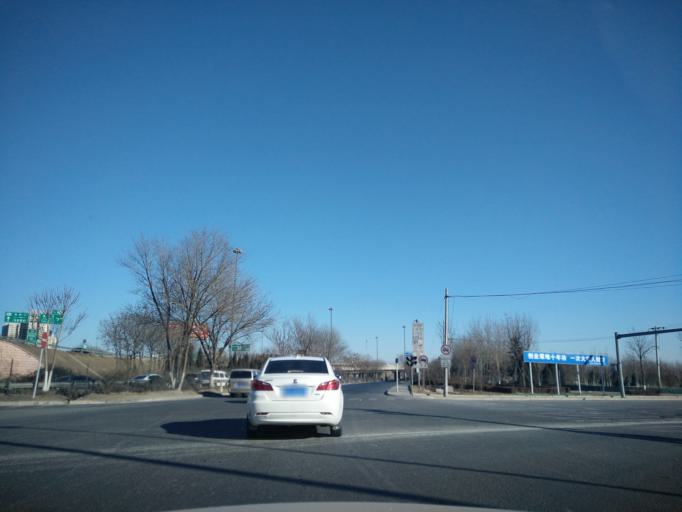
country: CN
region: Beijing
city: Xihongmen
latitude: 39.7747
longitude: 116.3362
